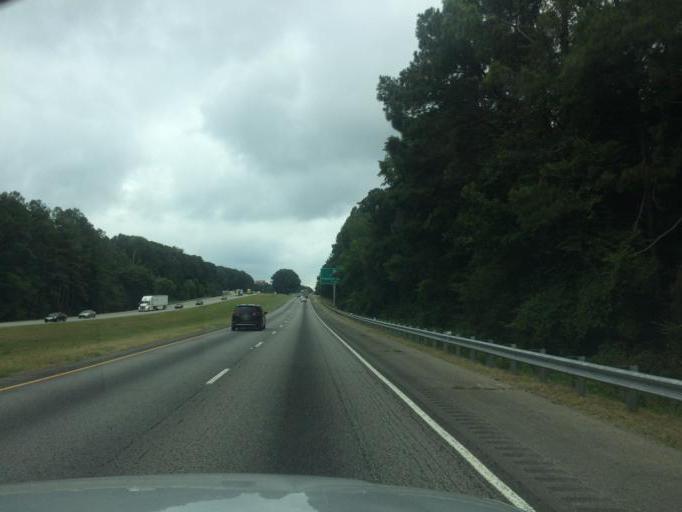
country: US
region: Georgia
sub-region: Franklin County
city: Carnesville
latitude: 34.3572
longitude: -83.3004
